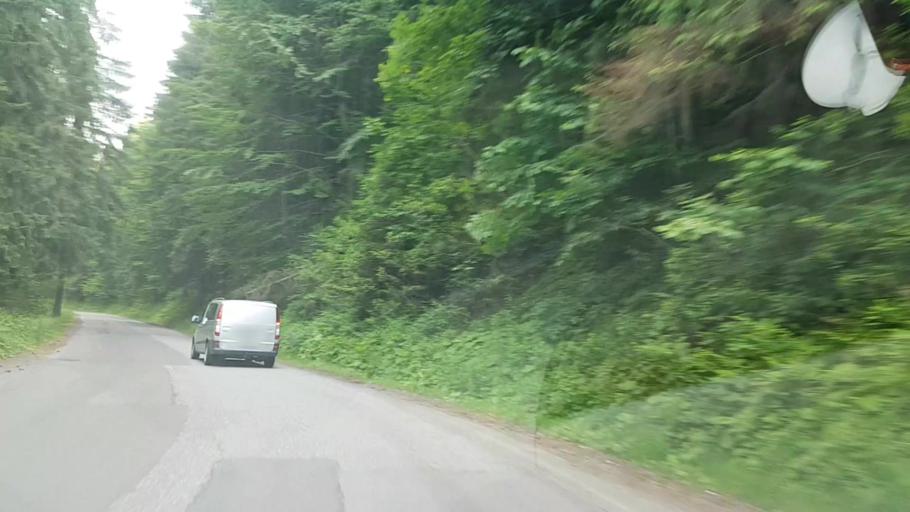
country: RO
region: Harghita
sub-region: Comuna Remetea
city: Remetea
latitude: 46.6740
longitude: 25.3389
